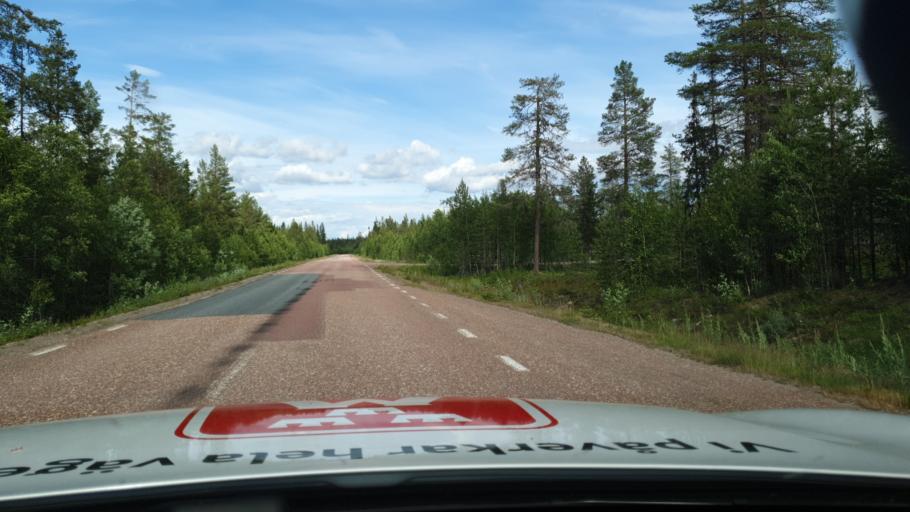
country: SE
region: Dalarna
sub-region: Alvdalens Kommun
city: AElvdalen
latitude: 61.7636
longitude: 13.4688
